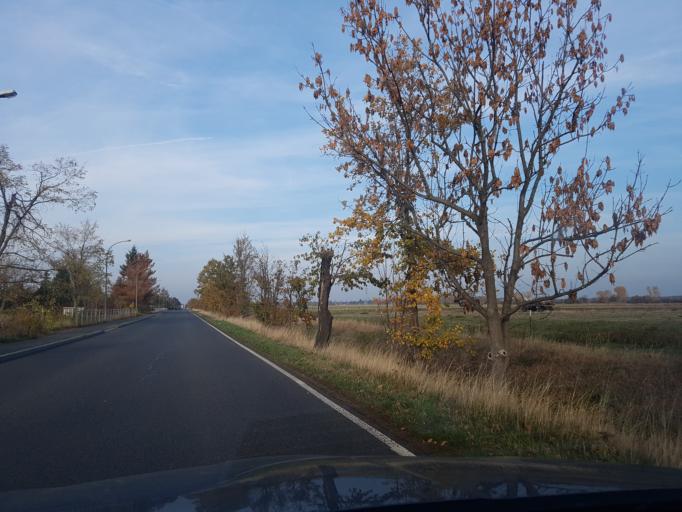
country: DE
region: Brandenburg
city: Falkenberg
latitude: 51.5636
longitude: 13.2281
